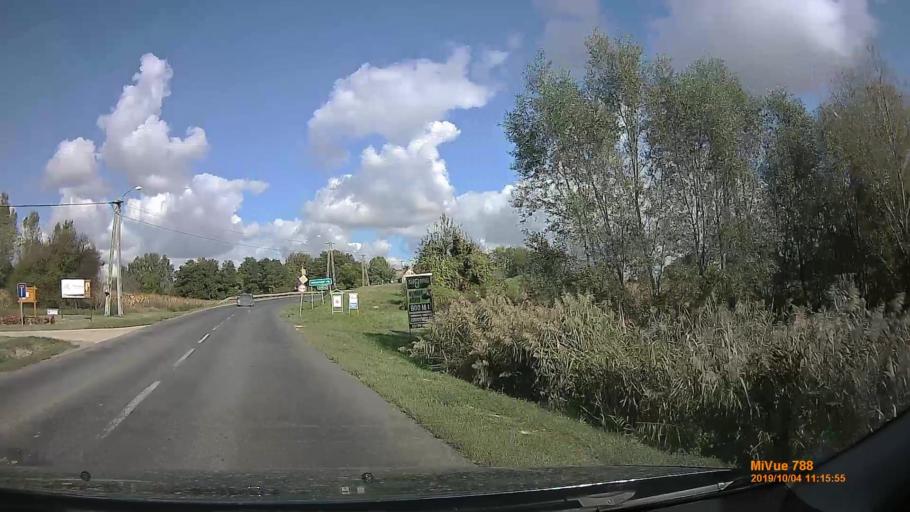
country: HU
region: Somogy
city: Kaposvar
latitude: 46.4514
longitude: 17.8045
